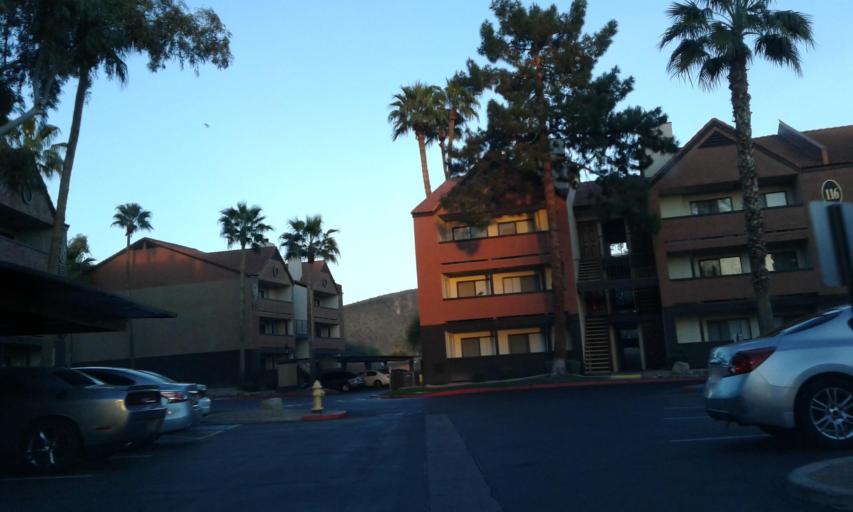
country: US
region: Arizona
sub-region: Maricopa County
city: Glendale
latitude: 33.5959
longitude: -112.1145
